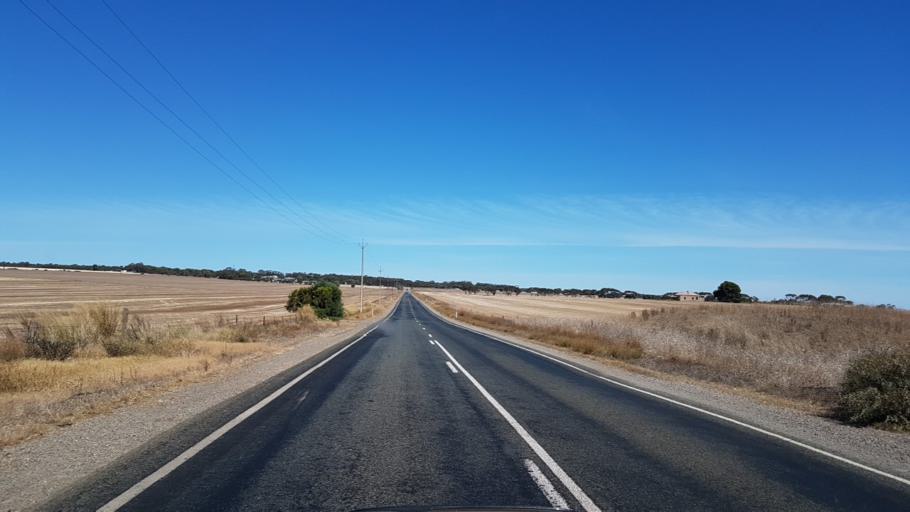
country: AU
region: South Australia
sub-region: Yorke Peninsula
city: Maitland
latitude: -34.3526
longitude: 137.6631
